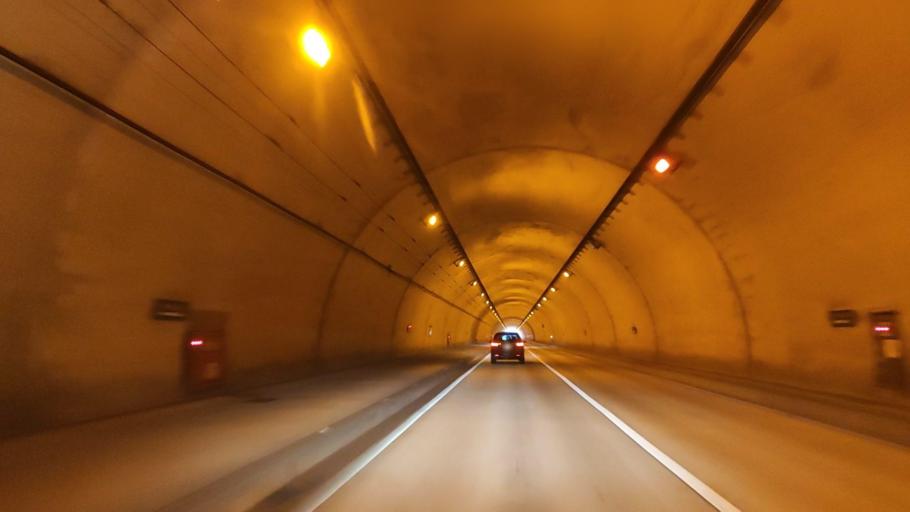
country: JP
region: Ehime
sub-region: Shikoku-chuo Shi
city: Matsuyama
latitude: 33.8837
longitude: 132.7093
